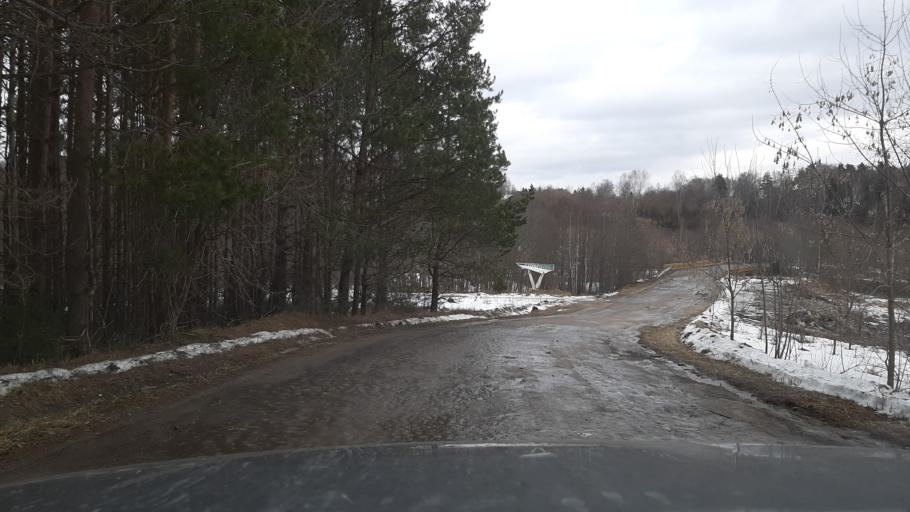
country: RU
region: Ivanovo
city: Teykovo
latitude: 56.8943
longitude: 40.6621
